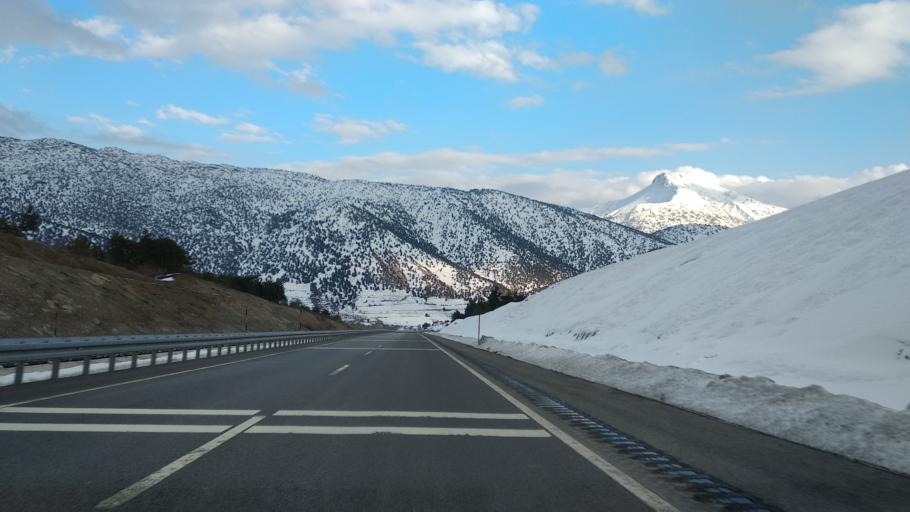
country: TR
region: Kahramanmaras
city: Goksun
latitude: 37.9051
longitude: 36.6015
